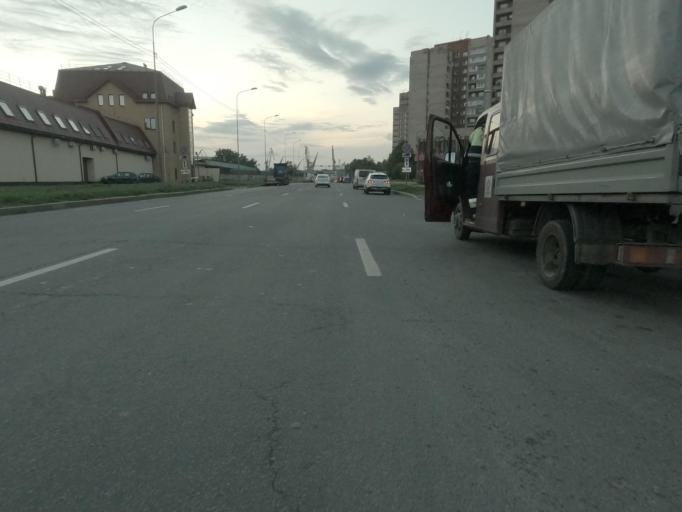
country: RU
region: St.-Petersburg
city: Vasyl'evsky Ostrov
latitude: 59.9063
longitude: 30.2439
